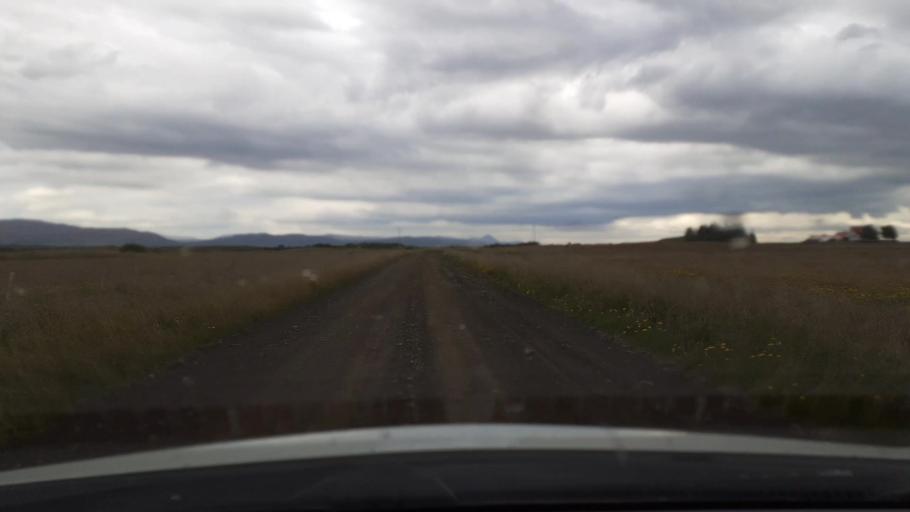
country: IS
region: West
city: Borgarnes
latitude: 64.6297
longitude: -21.9225
